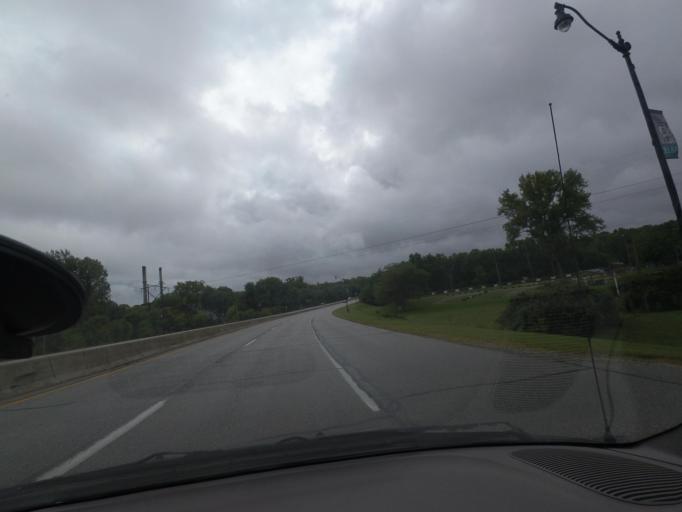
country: US
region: Indiana
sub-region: Montgomery County
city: Crawfordsville
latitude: 40.0510
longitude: -86.9018
